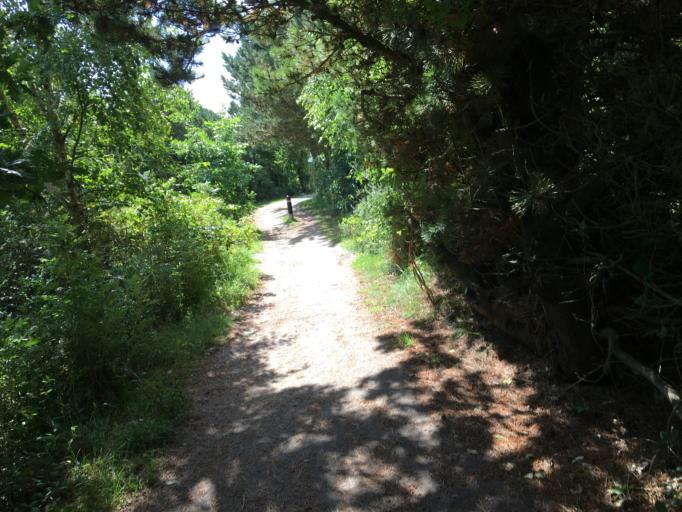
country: DK
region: Central Jutland
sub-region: Ringkobing-Skjern Kommune
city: Hvide Sande
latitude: 55.8659
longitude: 8.1739
